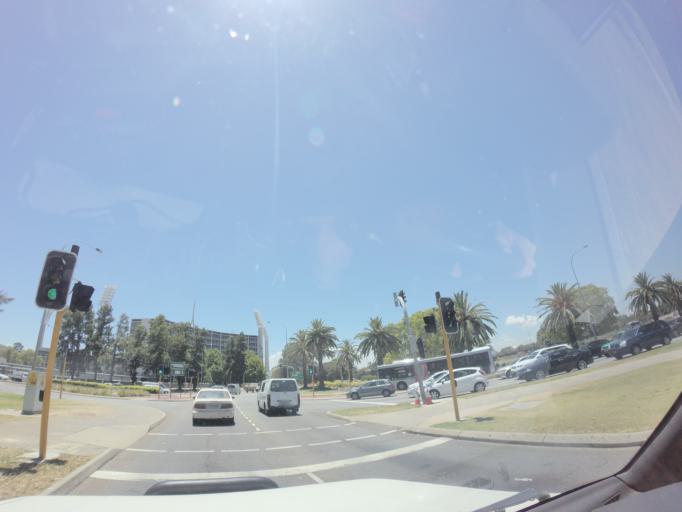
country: AU
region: Western Australia
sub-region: City of Perth
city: East Perth
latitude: -31.9626
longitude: 115.8783
